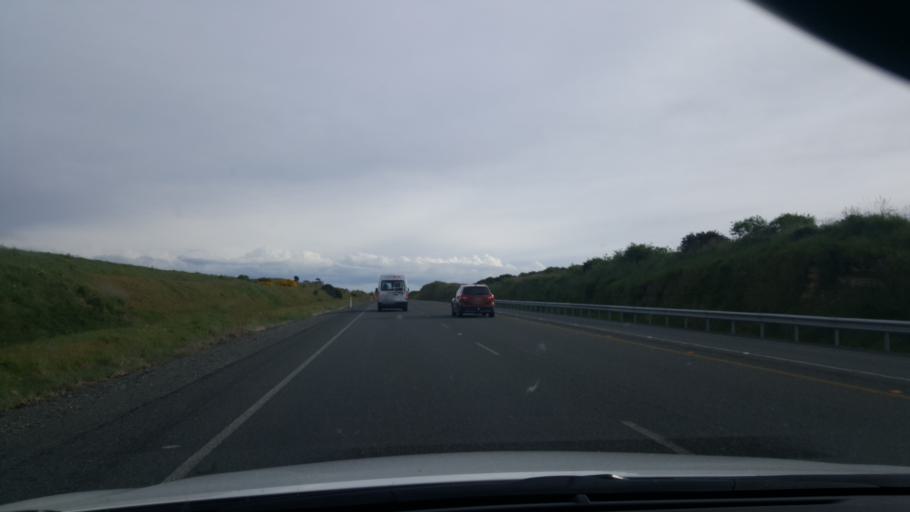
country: NZ
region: Waikato
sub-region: Taupo District
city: Taupo
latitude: -38.6457
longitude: 176.0999
